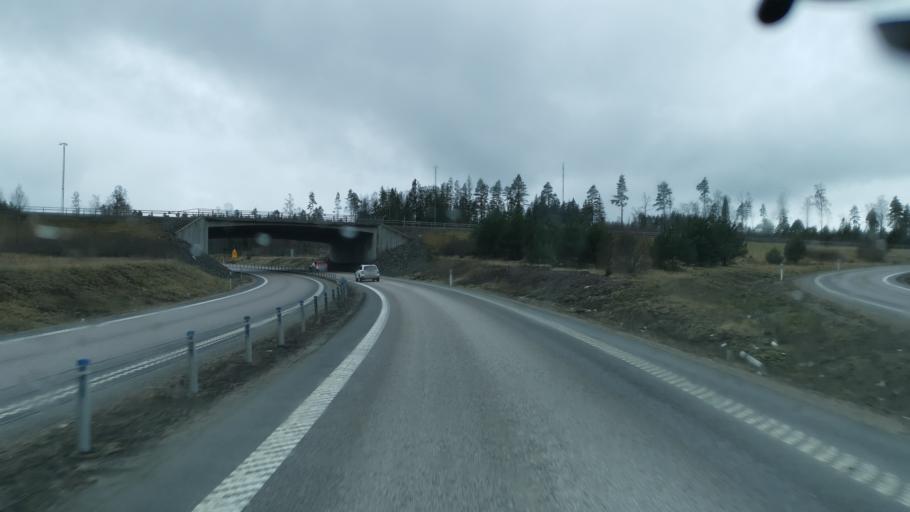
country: SE
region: Vaestra Goetaland
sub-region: Uddevalla Kommun
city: Uddevalla
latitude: 58.3370
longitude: 11.9858
